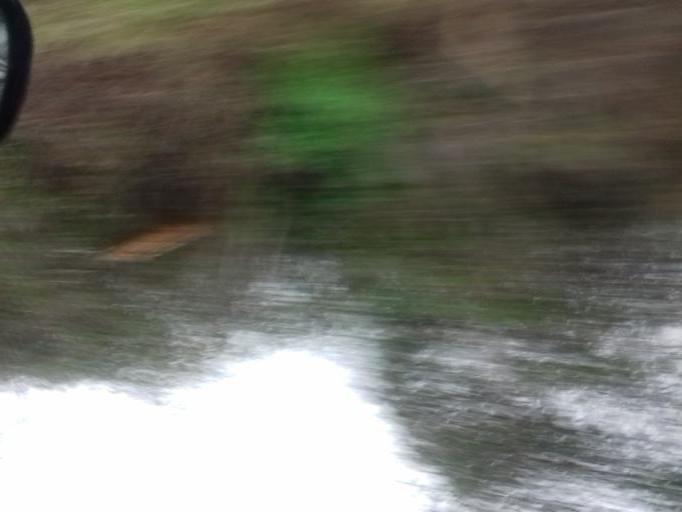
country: IE
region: Leinster
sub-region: Kilkenny
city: Graiguenamanagh
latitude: 52.5509
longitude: -6.9586
